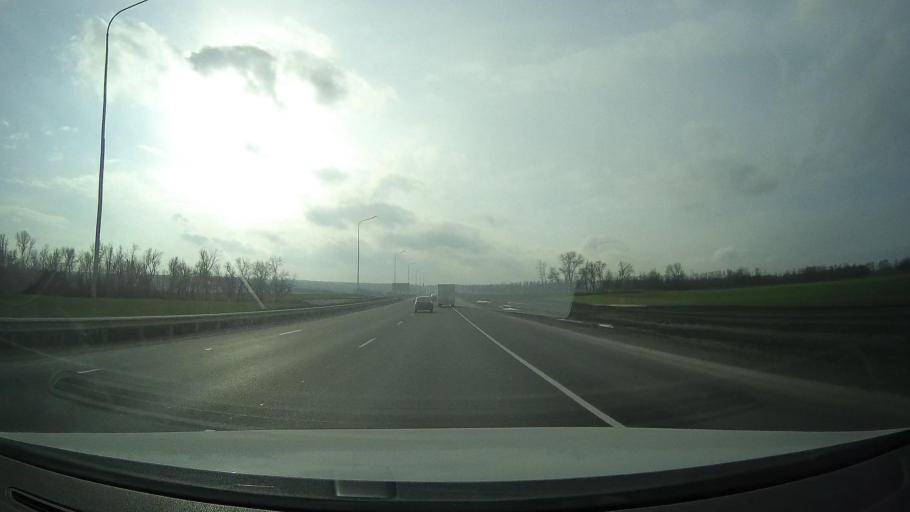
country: RU
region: Rostov
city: Grushevskaya
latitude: 47.4511
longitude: 39.8810
